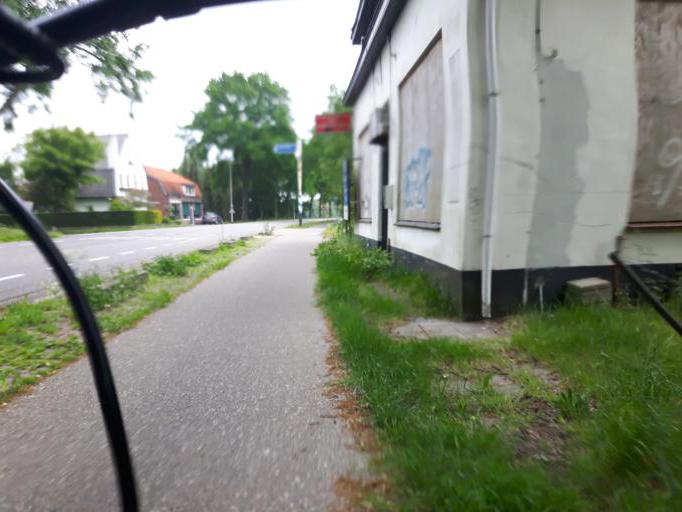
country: NL
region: North Brabant
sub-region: Gemeente Bergen op Zoom
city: Lepelstraat
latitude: 51.5475
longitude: 4.2880
